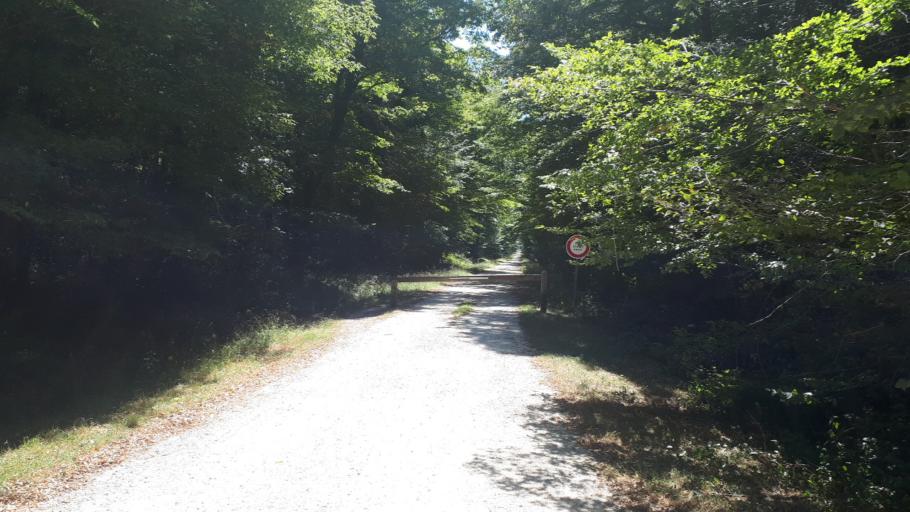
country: FR
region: Centre
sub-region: Departement du Loir-et-Cher
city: Vineuil
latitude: 47.5617
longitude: 1.4096
